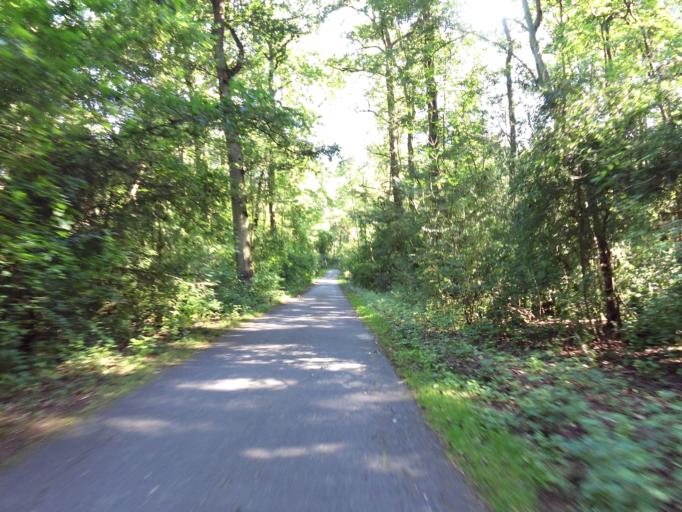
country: DE
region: Hesse
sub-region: Regierungsbezirk Darmstadt
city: Stockstadt am Rhein
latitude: 49.8260
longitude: 8.4610
